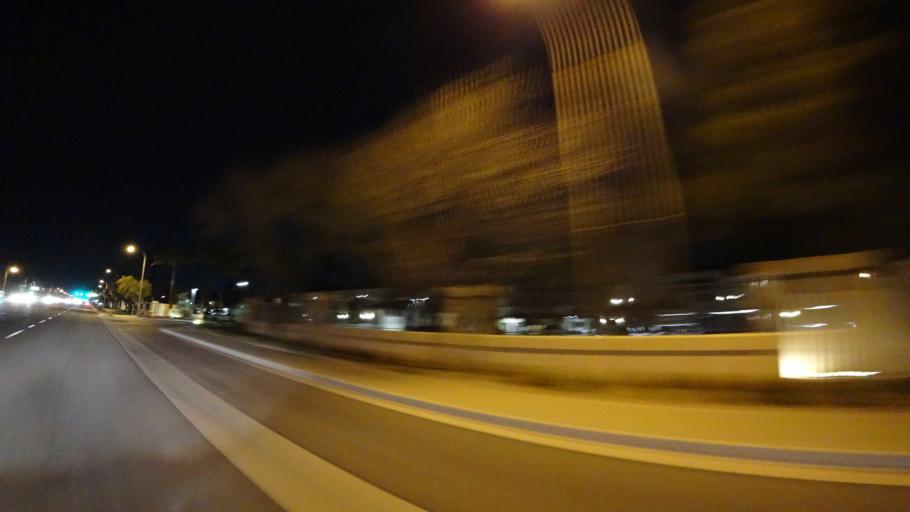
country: US
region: Arizona
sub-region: Maricopa County
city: Guadalupe
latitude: 33.3783
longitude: -111.9496
